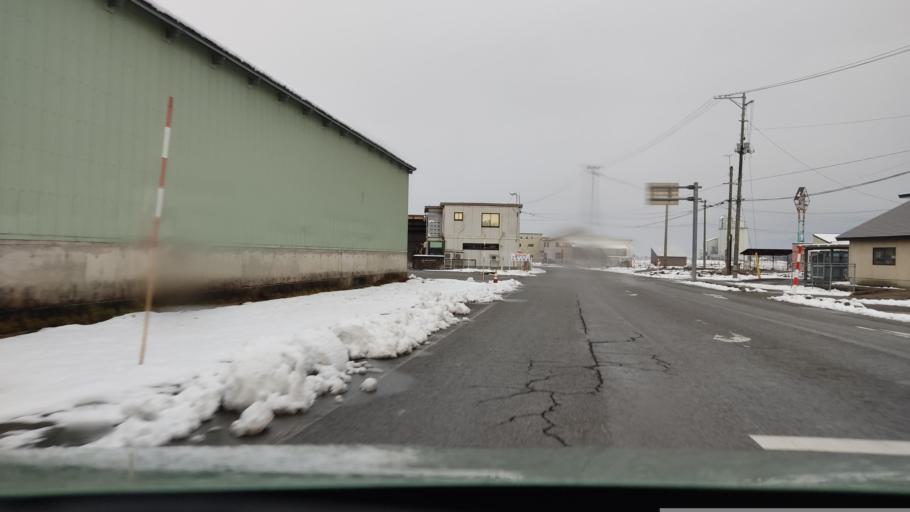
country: JP
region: Akita
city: Omagari
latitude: 39.4231
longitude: 140.5350
